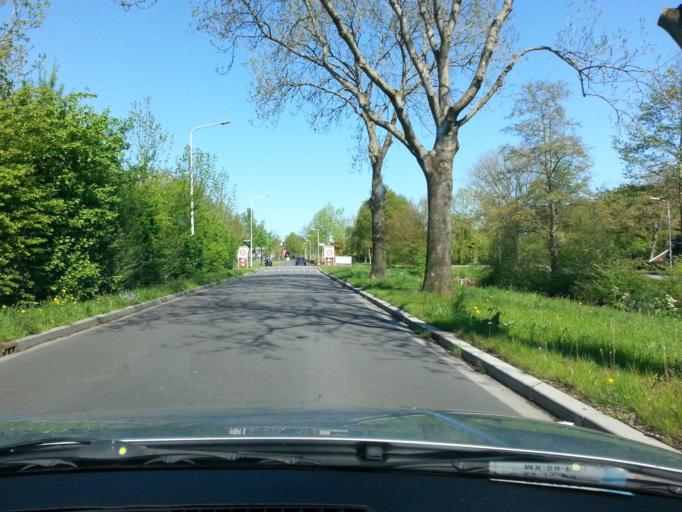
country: NL
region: Friesland
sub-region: Gemeente Achtkarspelen
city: Buitenpost
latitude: 53.2472
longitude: 6.1518
